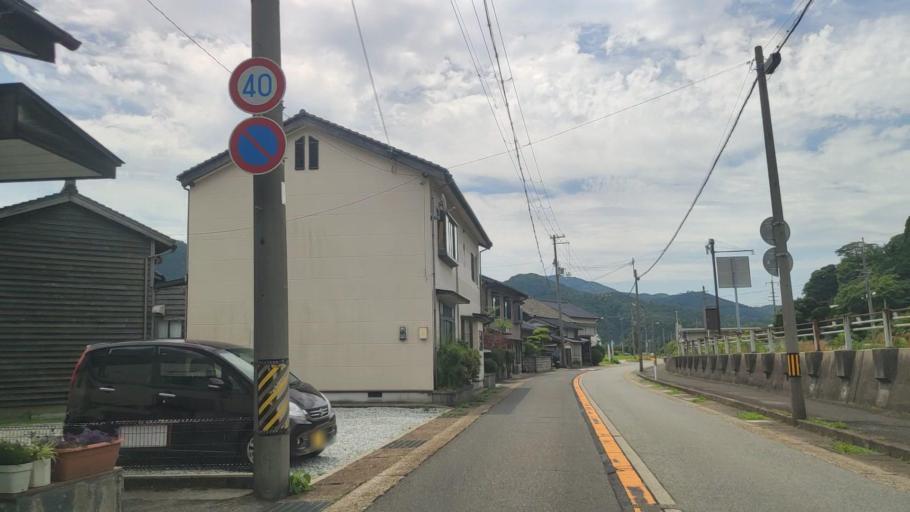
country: JP
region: Hyogo
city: Toyooka
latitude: 35.6497
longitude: 134.7570
